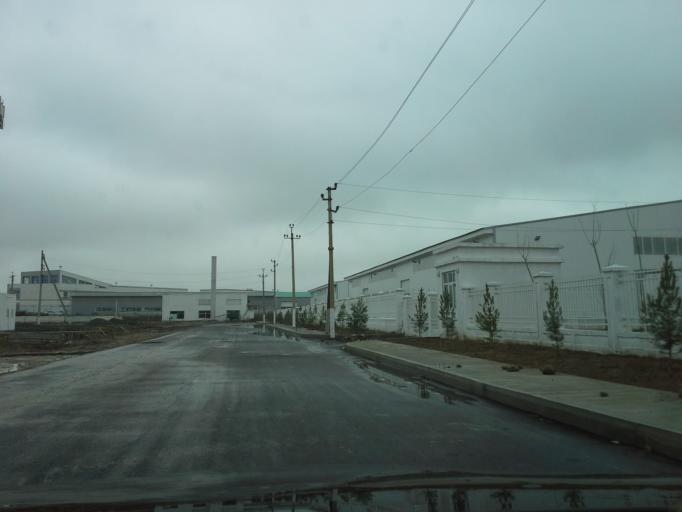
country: TM
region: Ahal
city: Ashgabat
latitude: 37.9517
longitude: 58.4312
